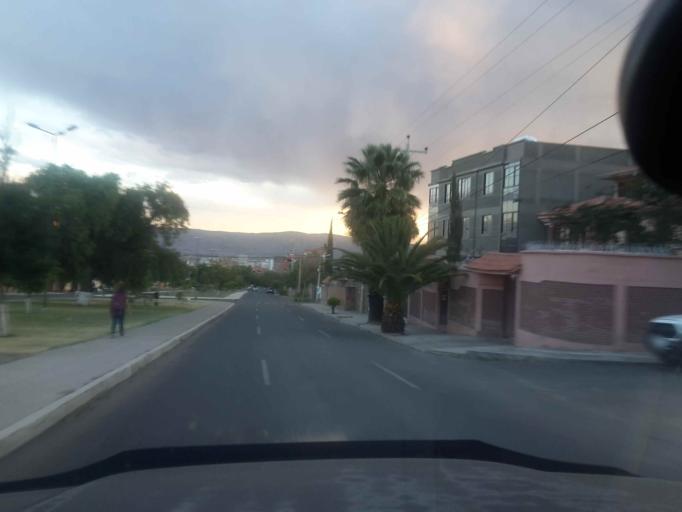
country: BO
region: Cochabamba
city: Cochabamba
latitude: -17.3577
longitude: -66.1691
